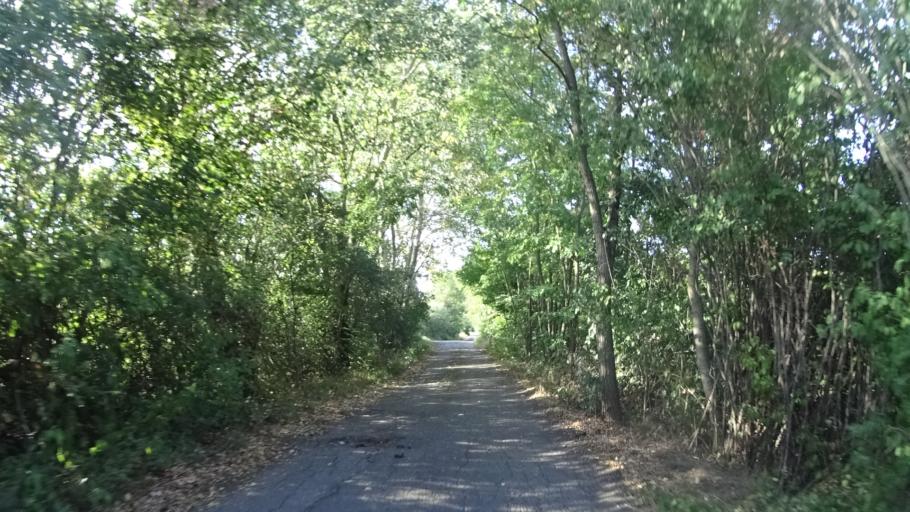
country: AT
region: Lower Austria
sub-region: Politischer Bezirk Mistelbach
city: Rabensburg
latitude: 48.6033
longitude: 16.9490
